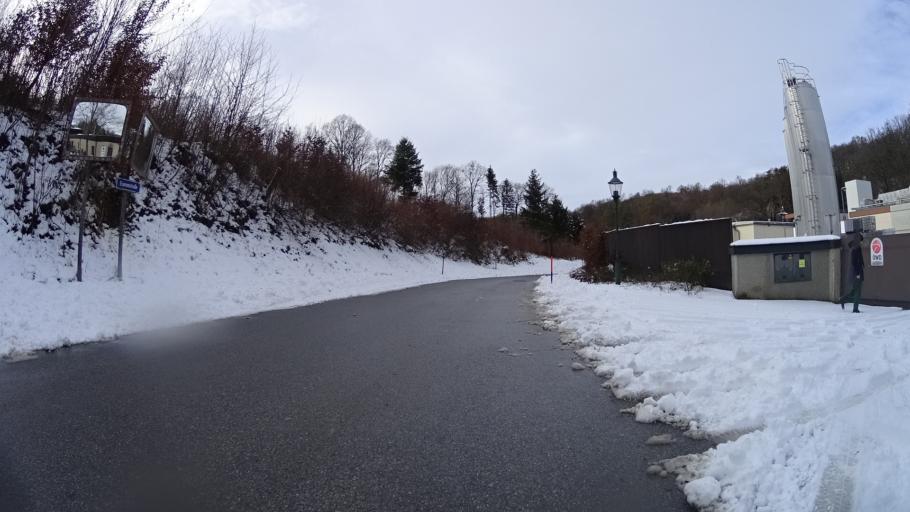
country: AT
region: Lower Austria
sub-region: Politischer Bezirk Korneuburg
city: Niederhollabrunn
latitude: 48.4105
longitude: 16.3098
